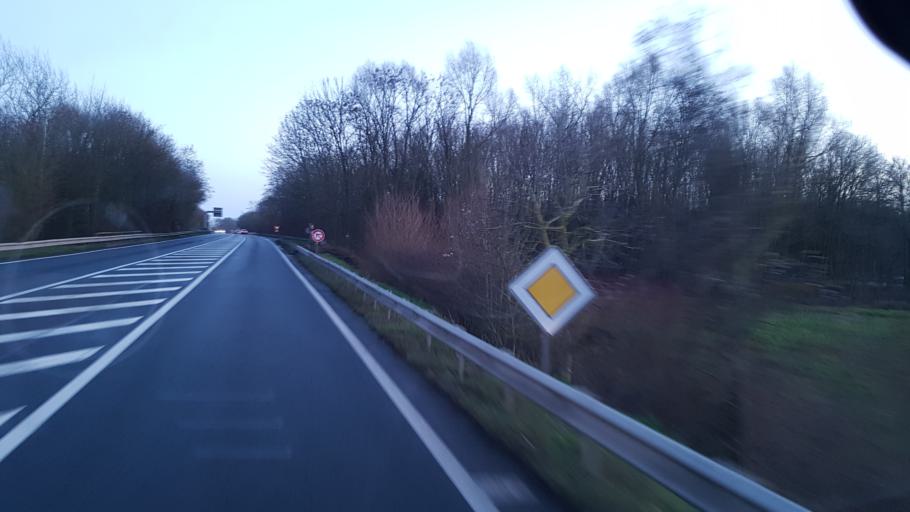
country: FR
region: Nord-Pas-de-Calais
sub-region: Departement du Nord
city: Cuincy
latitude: 50.3583
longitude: 3.0447
